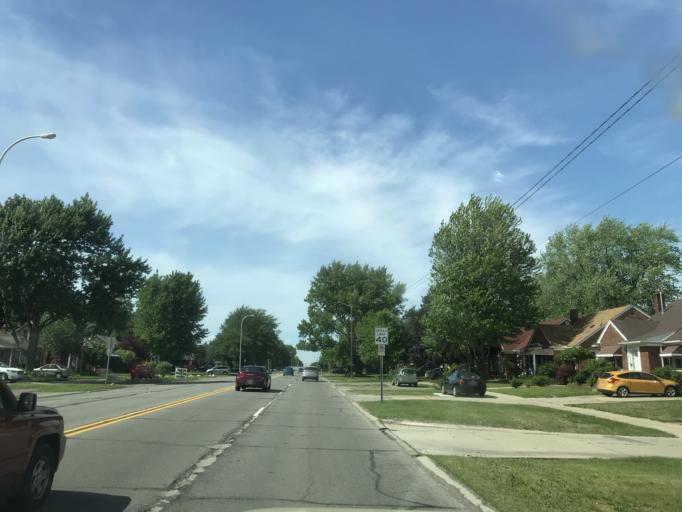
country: US
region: Michigan
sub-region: Wayne County
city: Redford
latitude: 42.3649
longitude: -83.3132
